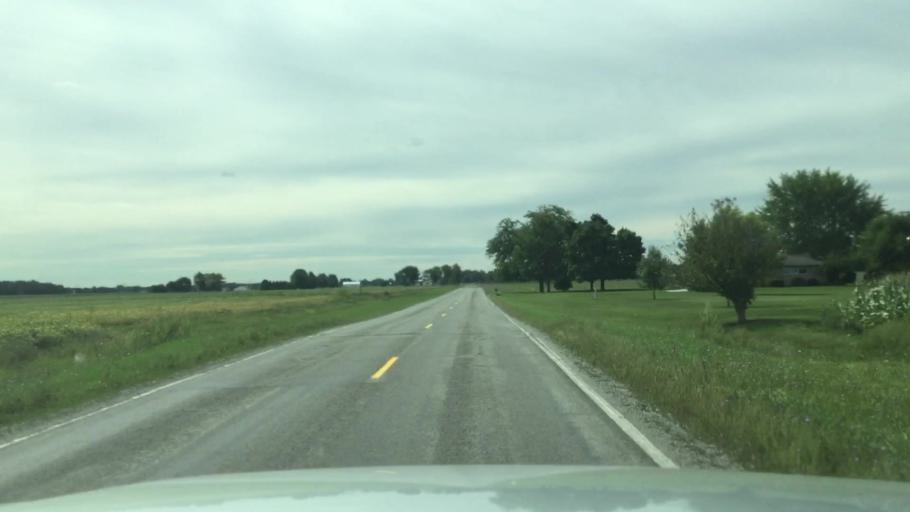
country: US
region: Michigan
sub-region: Genesee County
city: Montrose
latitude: 43.1398
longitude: -83.9883
